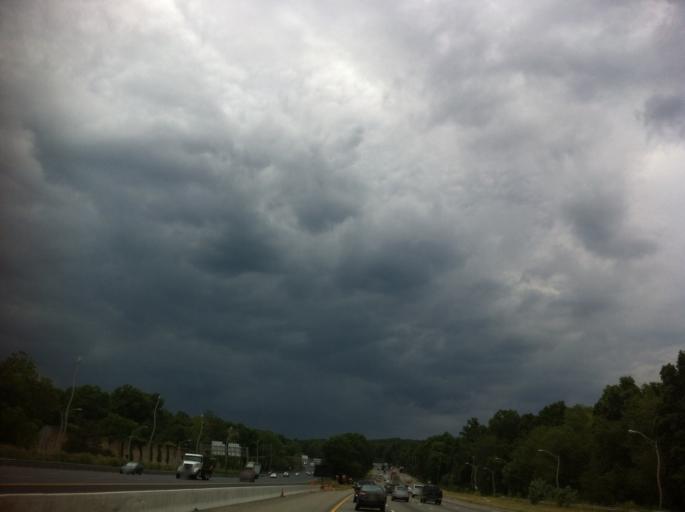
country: US
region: New Jersey
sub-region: Morris County
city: Parsippany
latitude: 40.8629
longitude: -74.4086
